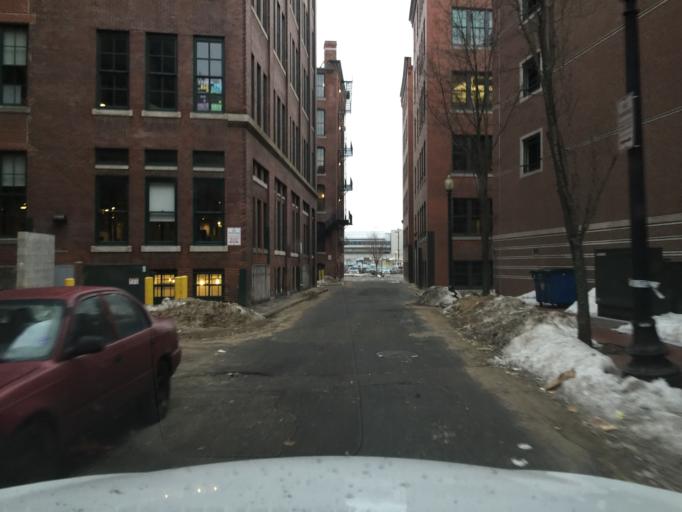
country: US
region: Massachusetts
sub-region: Suffolk County
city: Boston
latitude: 42.3494
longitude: -71.0505
